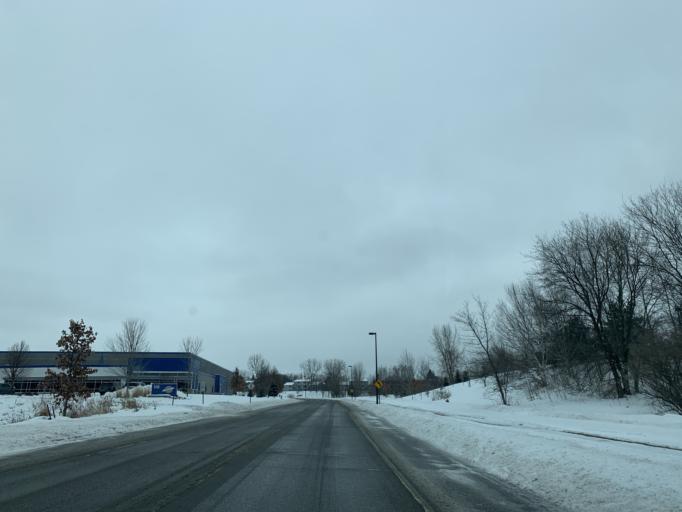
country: US
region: Minnesota
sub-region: Ramsey County
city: North Saint Paul
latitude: 45.0242
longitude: -92.9694
